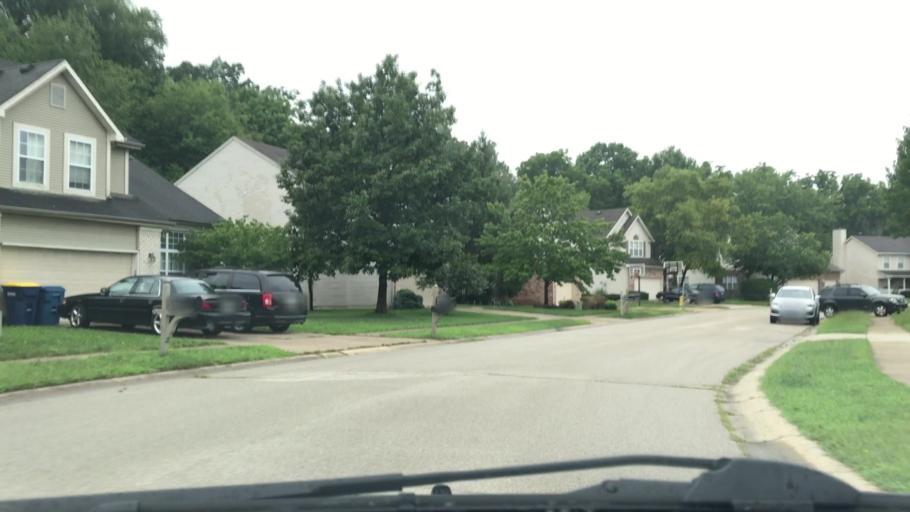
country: US
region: Indiana
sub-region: Hamilton County
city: Carmel
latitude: 39.9936
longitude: -86.0679
